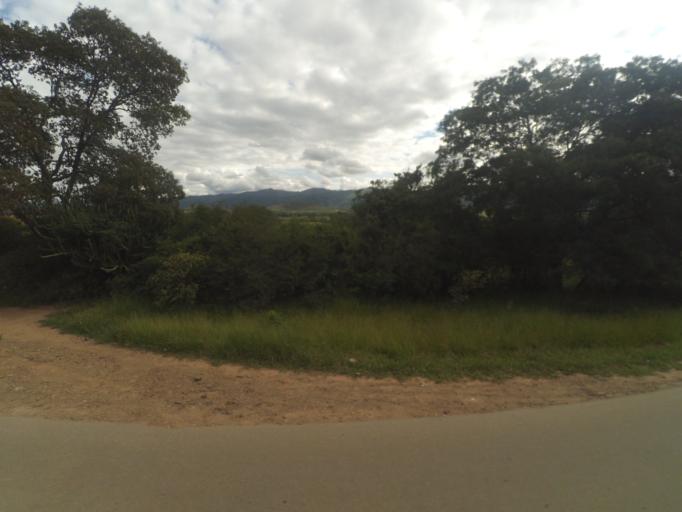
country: BO
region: Santa Cruz
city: Samaipata
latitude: -18.1605
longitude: -63.9153
